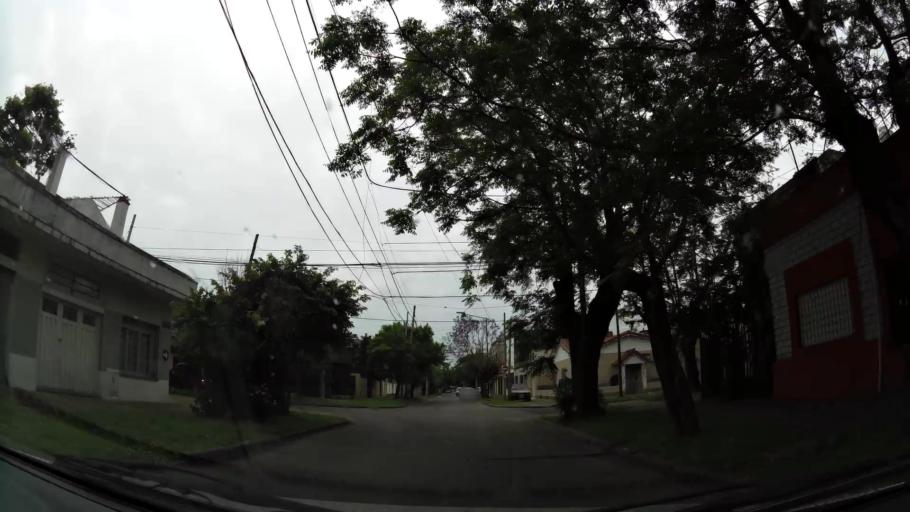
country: AR
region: Buenos Aires
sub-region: Partido de Lanus
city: Lanus
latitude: -34.7001
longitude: -58.4013
